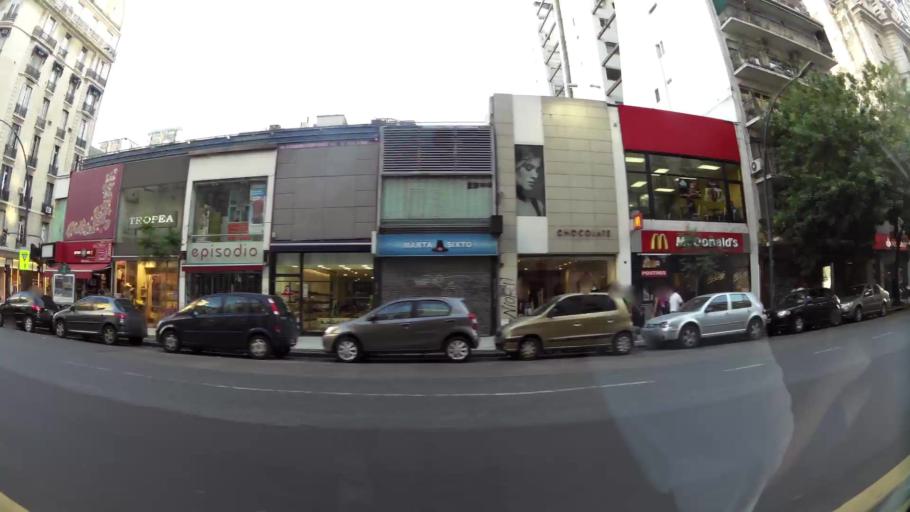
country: AR
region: Buenos Aires F.D.
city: Retiro
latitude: -34.5964
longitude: -58.3873
